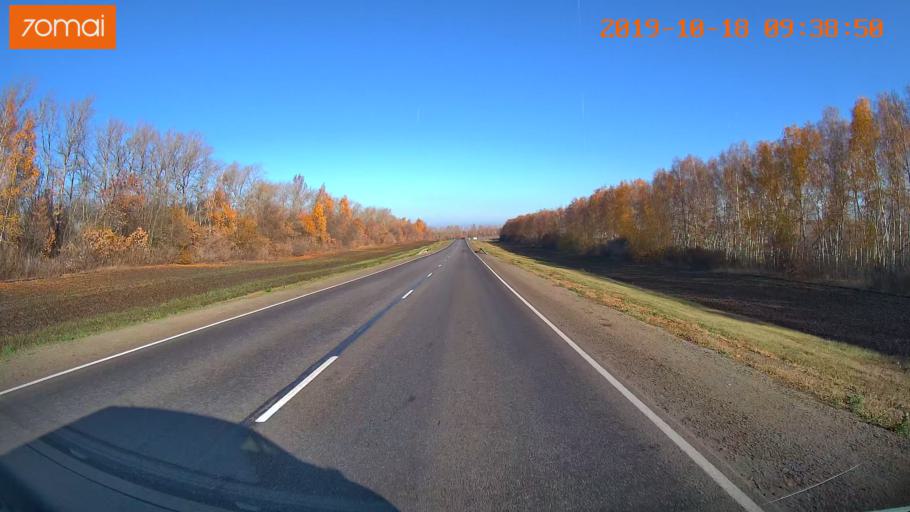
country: RU
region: Tula
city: Yefremov
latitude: 53.2439
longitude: 38.1355
